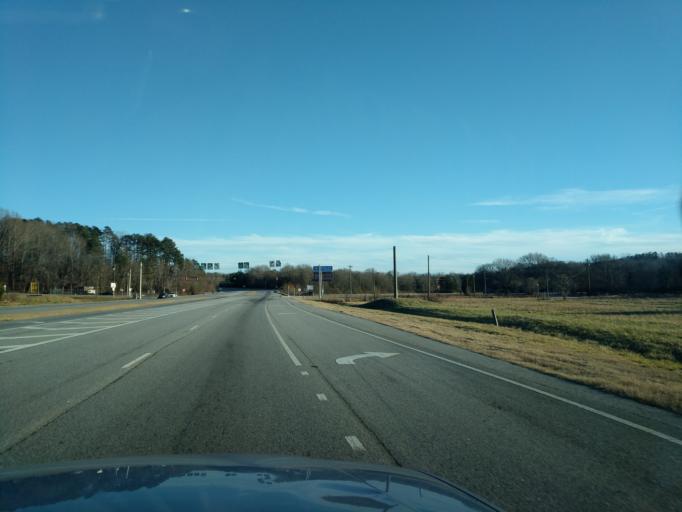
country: US
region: Georgia
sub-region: Stephens County
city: Toccoa
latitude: 34.5438
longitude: -83.3635
